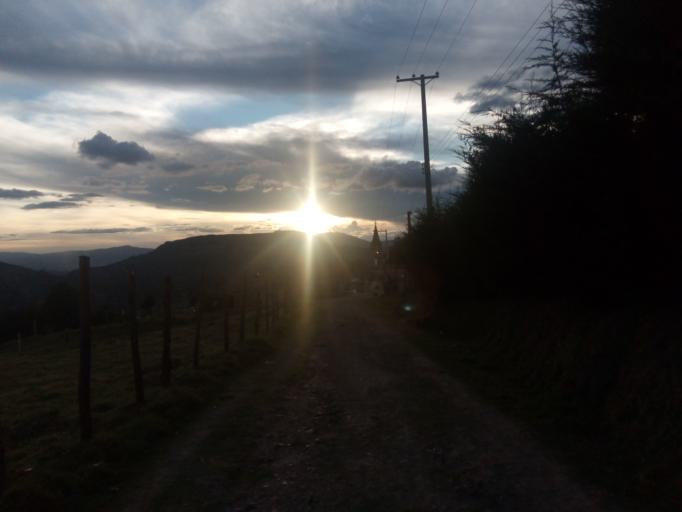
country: CO
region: Boyaca
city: Gameza
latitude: 5.8015
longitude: -72.8023
